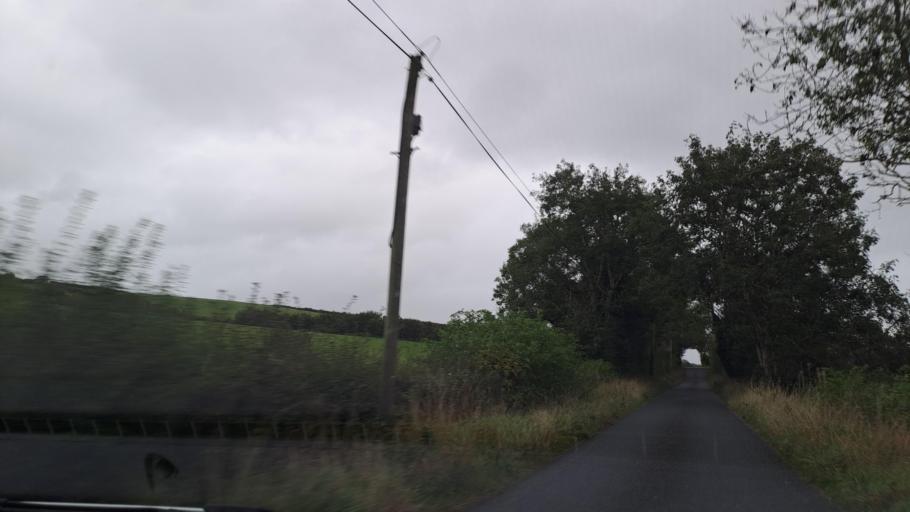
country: IE
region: Ulster
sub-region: An Cabhan
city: Kingscourt
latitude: 54.0019
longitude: -6.8527
